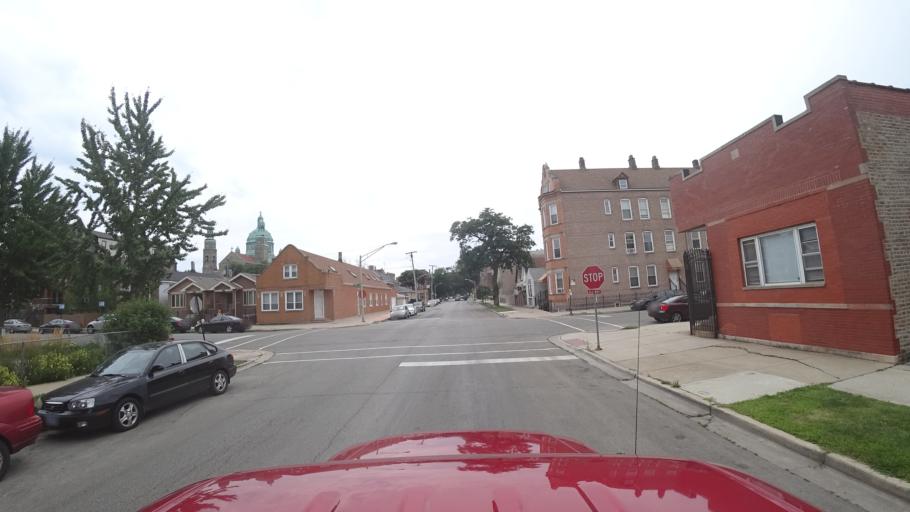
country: US
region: Illinois
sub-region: Cook County
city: Chicago
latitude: 41.8373
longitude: -87.6536
